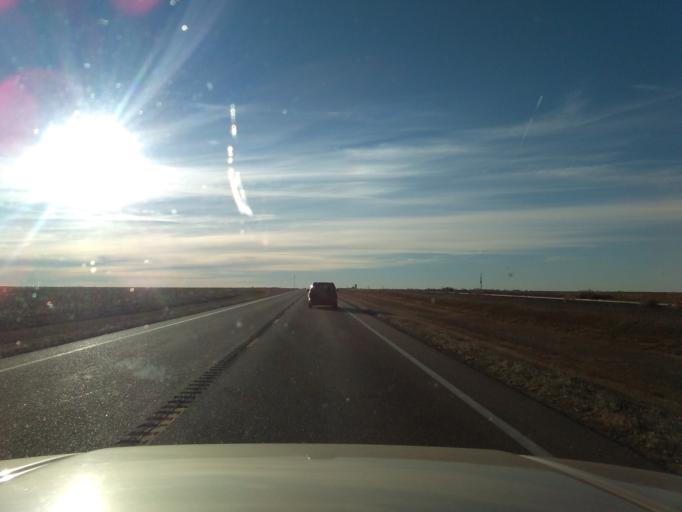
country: US
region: Kansas
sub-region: Thomas County
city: Colby
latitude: 39.4633
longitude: -100.7675
